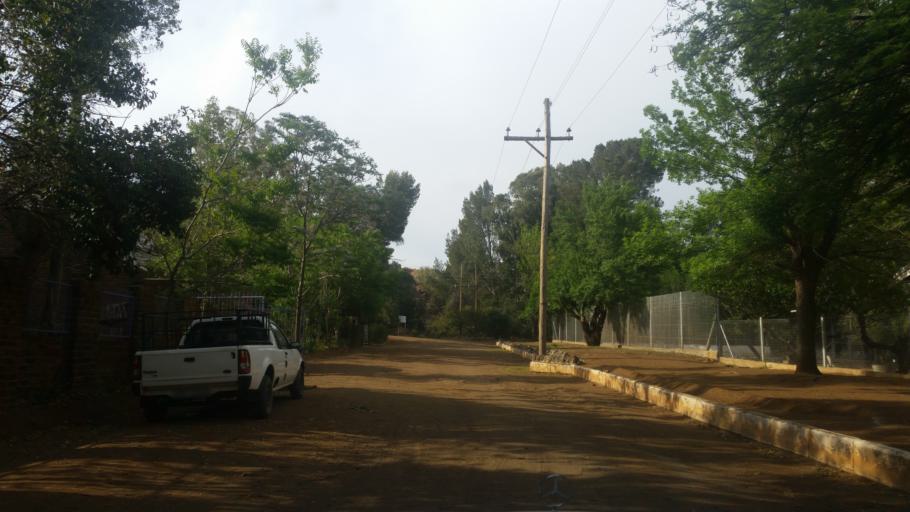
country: ZA
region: Orange Free State
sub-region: Xhariep District Municipality
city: Trompsburg
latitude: -30.4932
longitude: 25.9697
